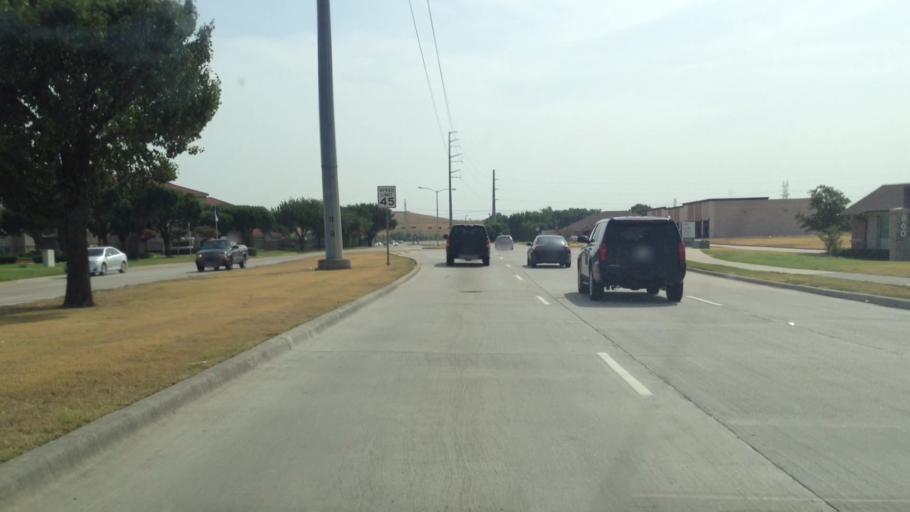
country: US
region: Texas
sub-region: Denton County
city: Lewisville
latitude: 33.0120
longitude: -96.9650
